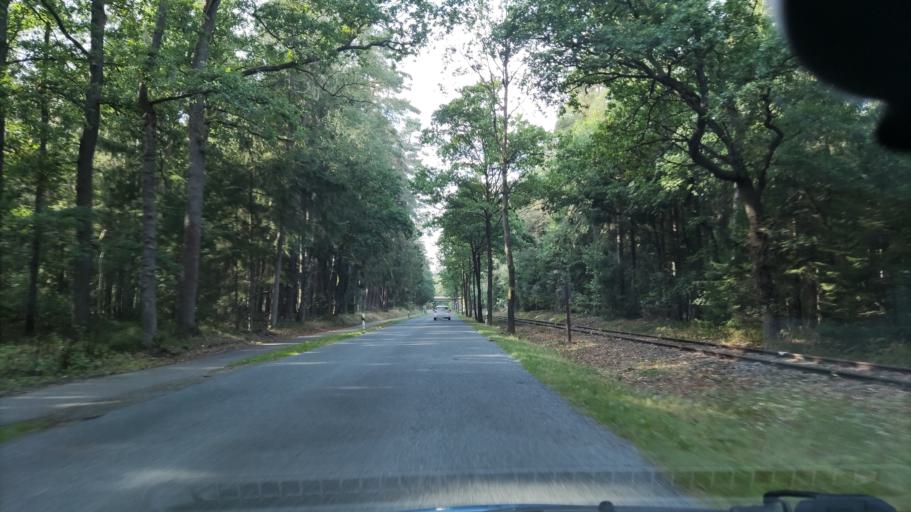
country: DE
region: Lower Saxony
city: Munster
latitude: 52.9835
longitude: 10.1297
